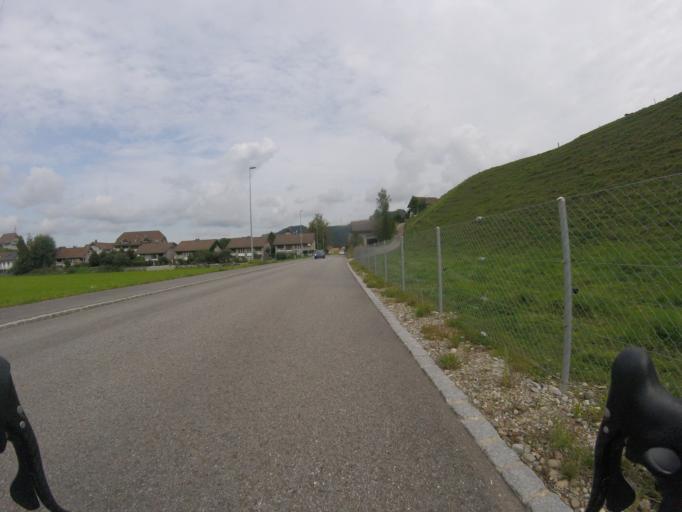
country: CH
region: Bern
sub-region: Emmental District
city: Lutzelfluh
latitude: 47.0005
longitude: 7.6797
